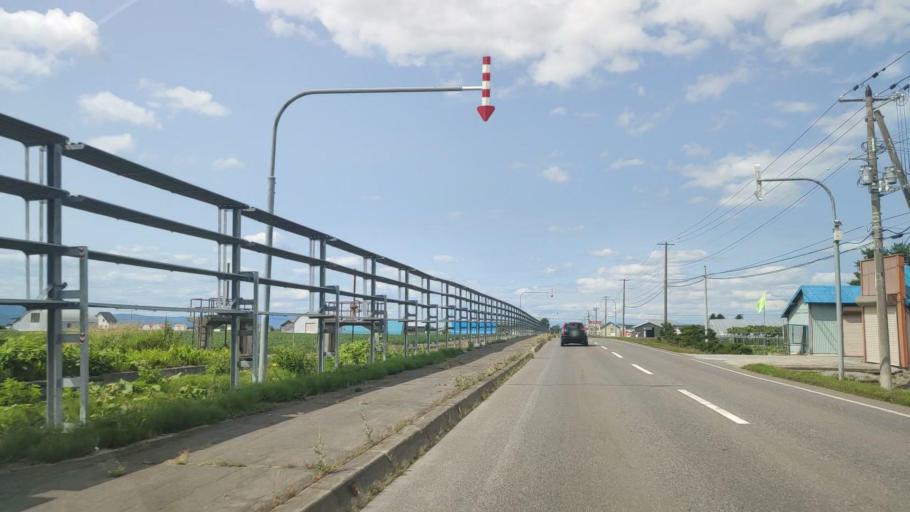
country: JP
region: Hokkaido
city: Nayoro
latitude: 44.1934
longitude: 142.4159
